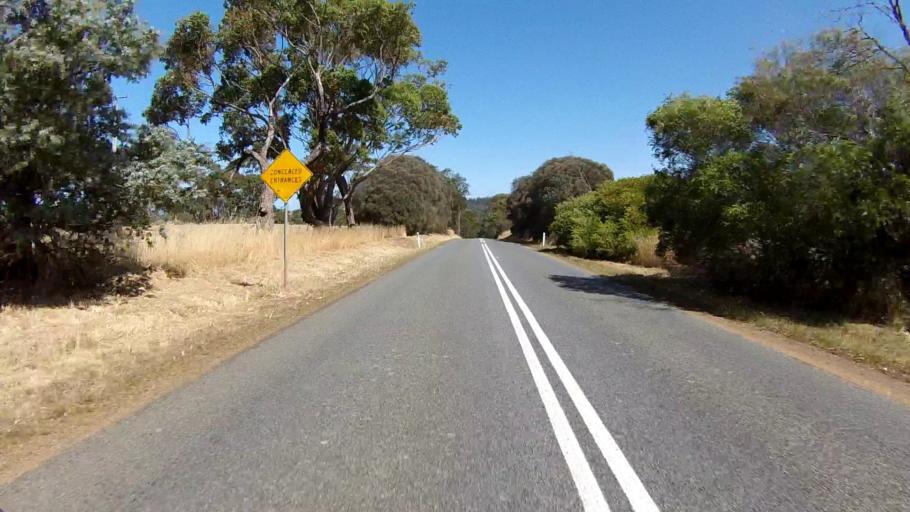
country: AU
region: Tasmania
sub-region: Sorell
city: Sorell
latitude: -42.2578
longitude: 148.0041
